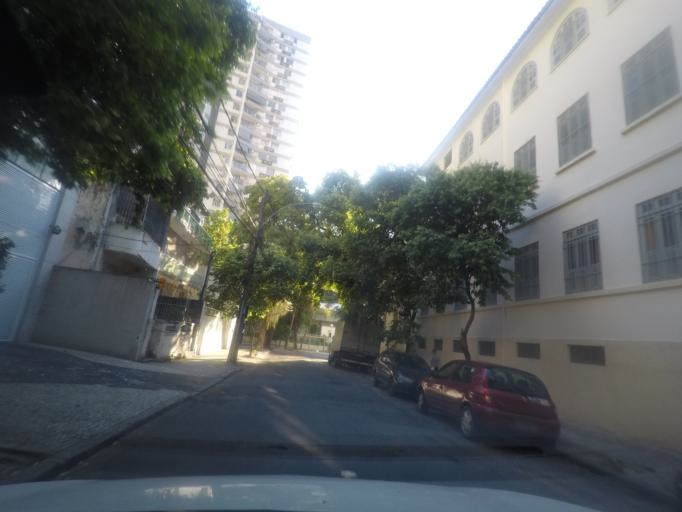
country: BR
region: Rio de Janeiro
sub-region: Rio De Janeiro
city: Rio de Janeiro
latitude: -22.9305
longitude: -43.1876
